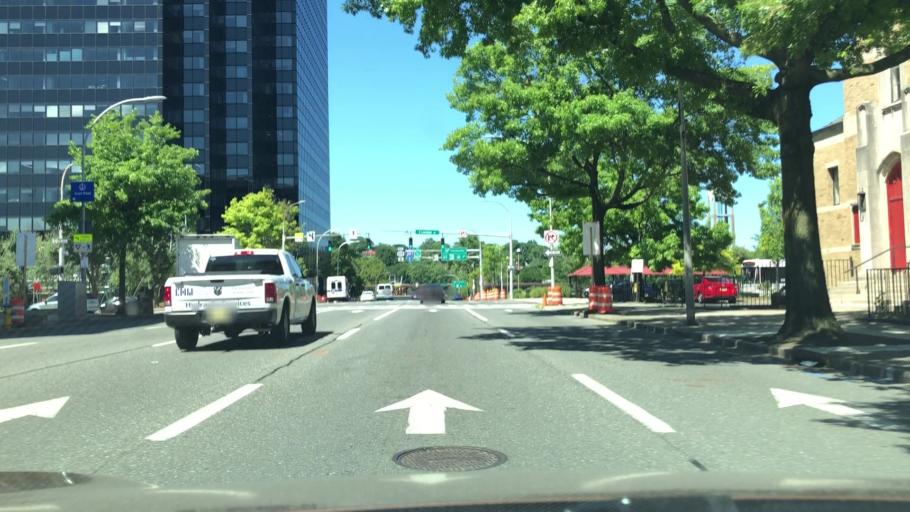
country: US
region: New York
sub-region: Westchester County
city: White Plains
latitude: 41.0328
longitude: -73.7719
